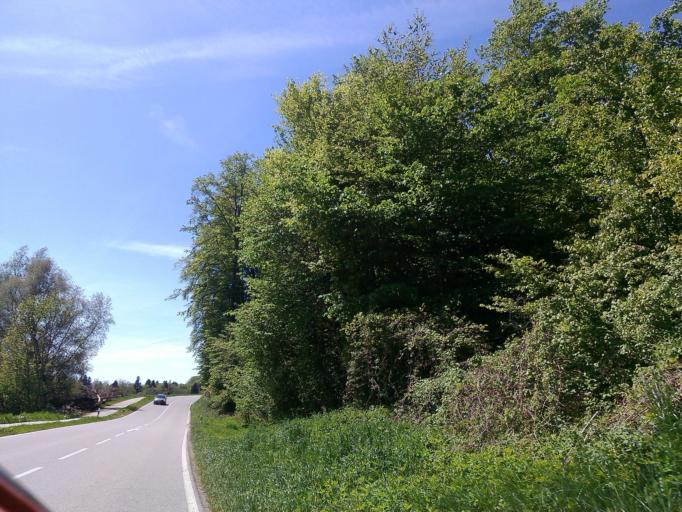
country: DE
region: Bavaria
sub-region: Upper Bavaria
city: Starnberg
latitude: 48.0240
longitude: 11.3591
